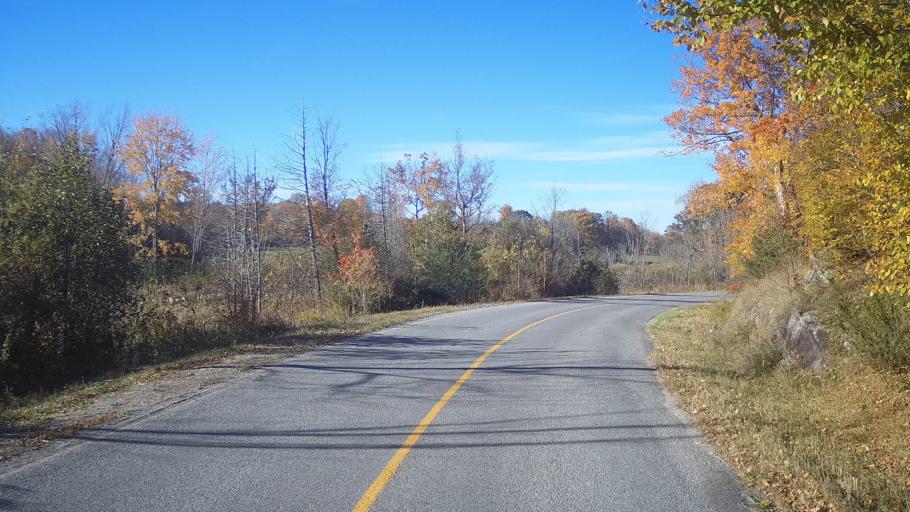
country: CA
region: Ontario
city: Kingston
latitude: 44.4583
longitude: -76.5017
